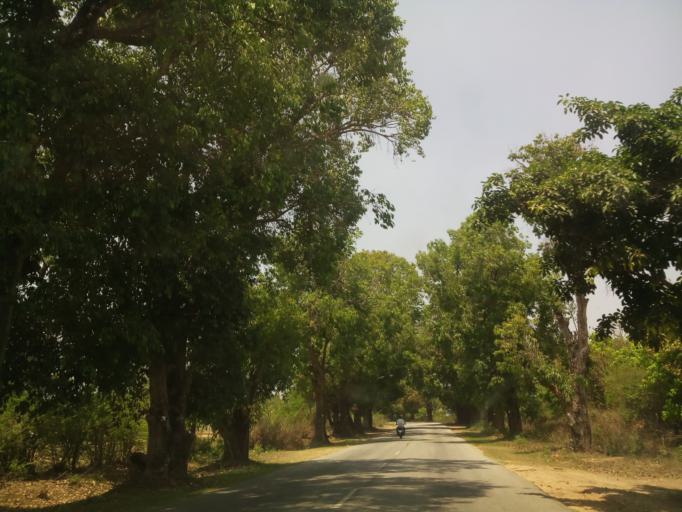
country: IN
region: Karnataka
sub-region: Hassan
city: Alur
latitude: 12.9504
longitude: 75.9296
